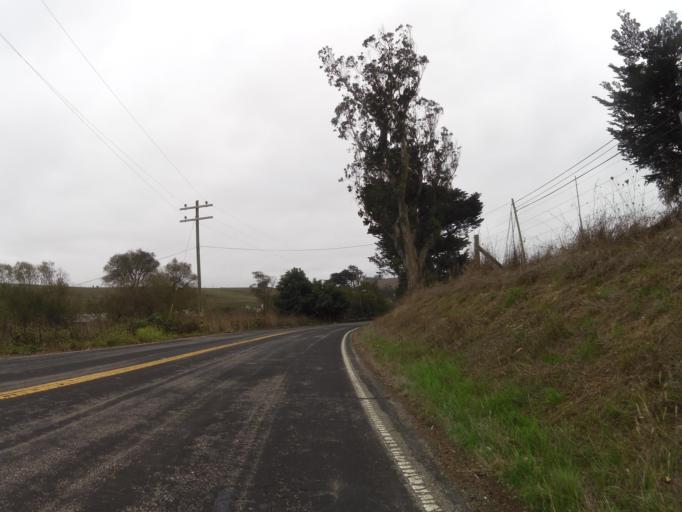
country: US
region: California
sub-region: Sonoma County
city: Occidental
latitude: 38.2741
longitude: -122.9003
